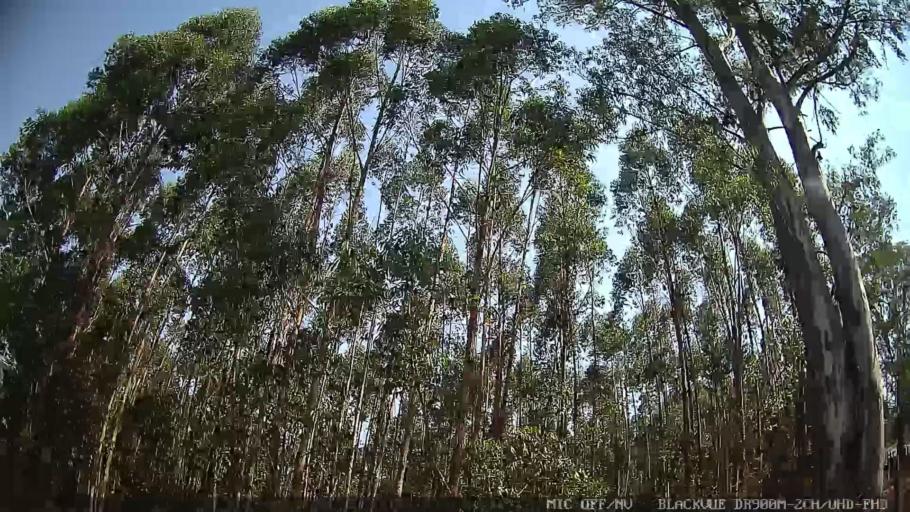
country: BR
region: Sao Paulo
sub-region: Itatiba
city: Itatiba
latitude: -23.0166
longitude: -46.9060
